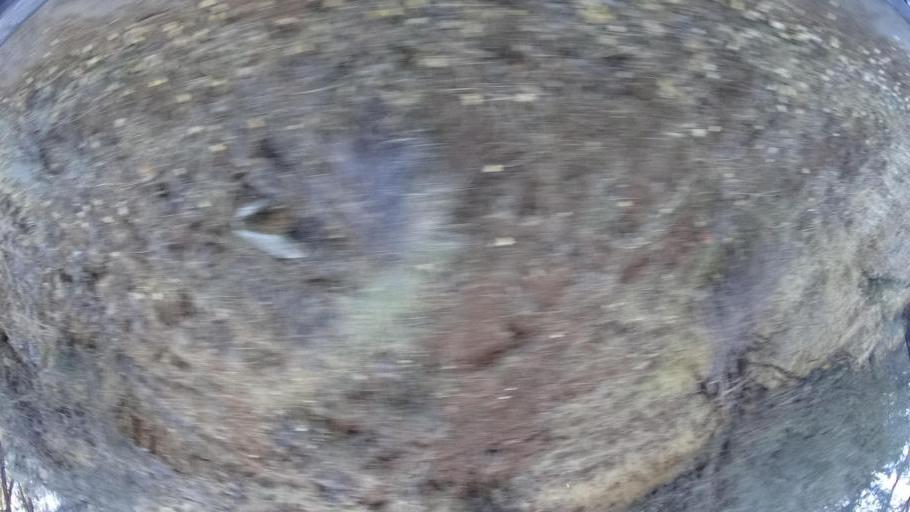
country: US
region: California
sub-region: Kern County
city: Golden Hills
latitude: 35.3061
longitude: -118.4440
